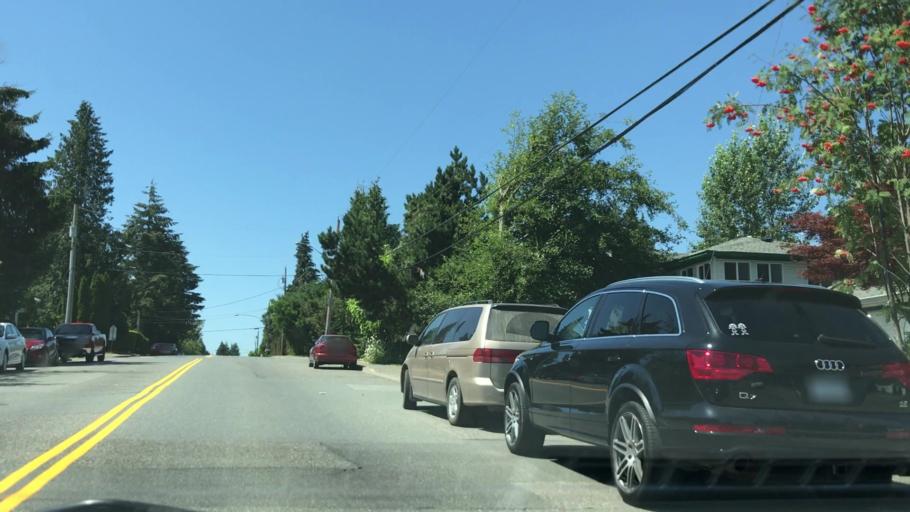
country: CA
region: British Columbia
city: Aldergrove
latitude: 49.0556
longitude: -122.4830
